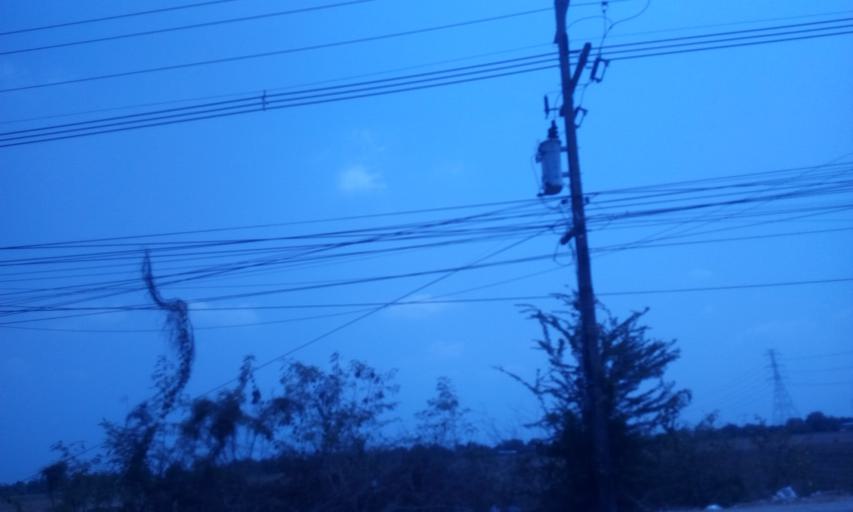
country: TH
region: Chachoengsao
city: Bang Nam Priao
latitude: 13.8285
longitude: 101.0557
